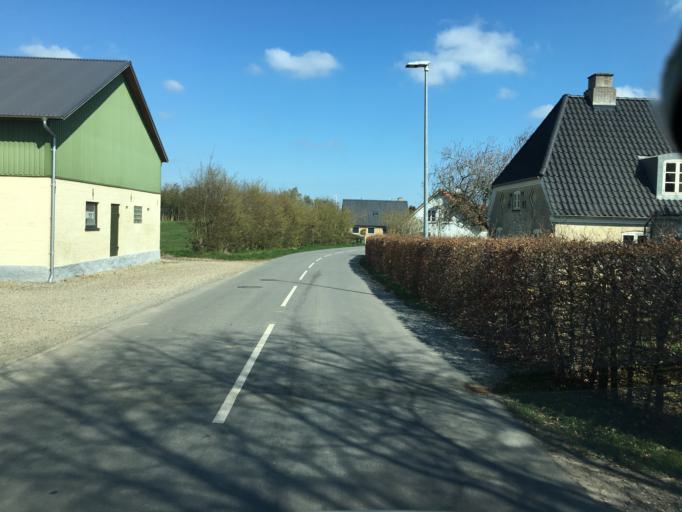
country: DK
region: South Denmark
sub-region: Sonderborg Kommune
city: Dybbol
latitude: 54.9537
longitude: 9.7252
